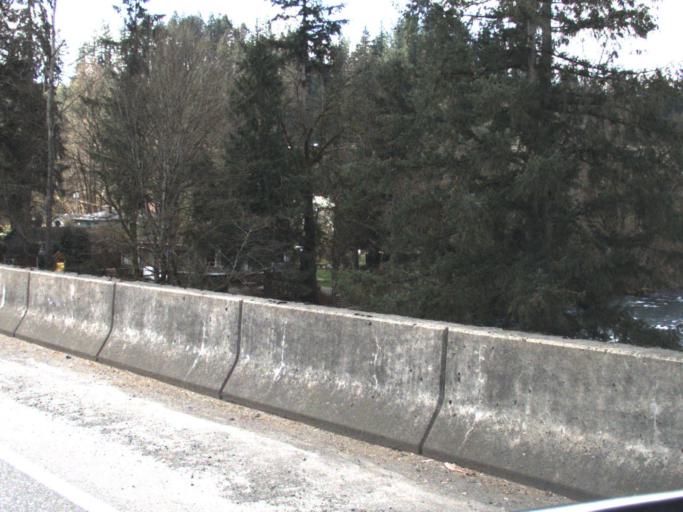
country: US
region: Washington
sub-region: King County
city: Maple Valley
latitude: 47.4063
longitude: -122.0389
